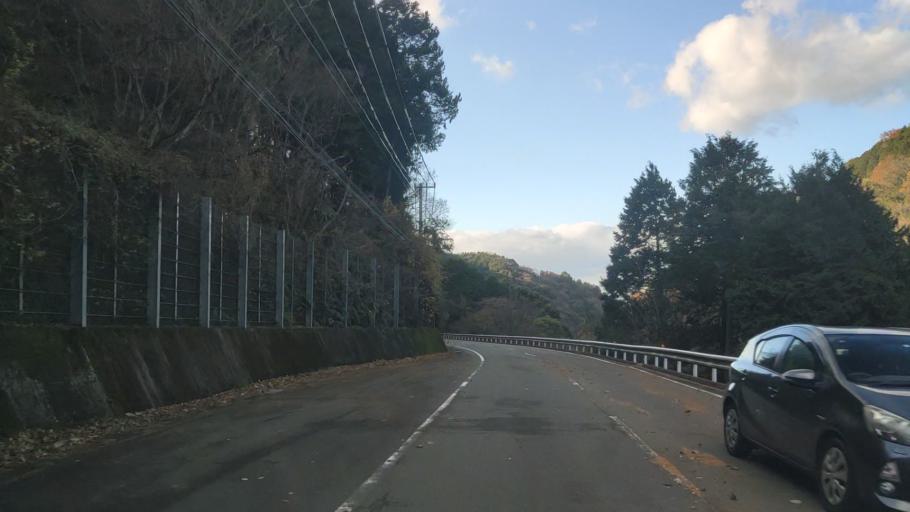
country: JP
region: Ehime
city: Saijo
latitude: 33.8780
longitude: 133.1366
